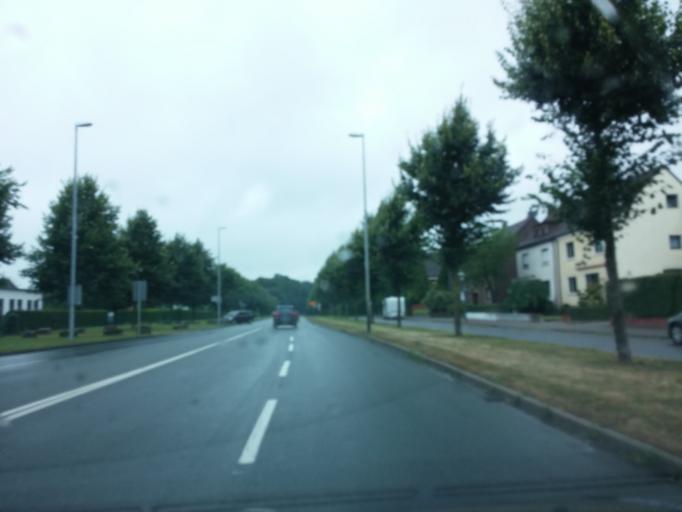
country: DE
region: North Rhine-Westphalia
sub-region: Regierungsbezirk Munster
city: Gladbeck
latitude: 51.5757
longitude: 7.0410
